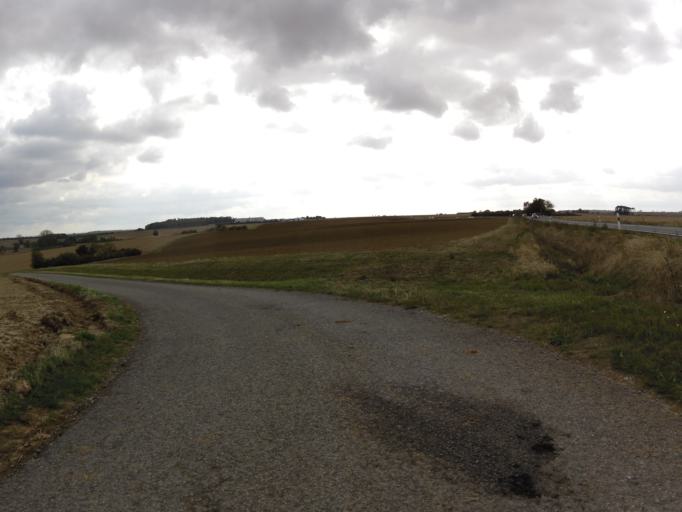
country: DE
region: Bavaria
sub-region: Regierungsbezirk Unterfranken
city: Reichenberg
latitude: 49.7079
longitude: 9.9409
